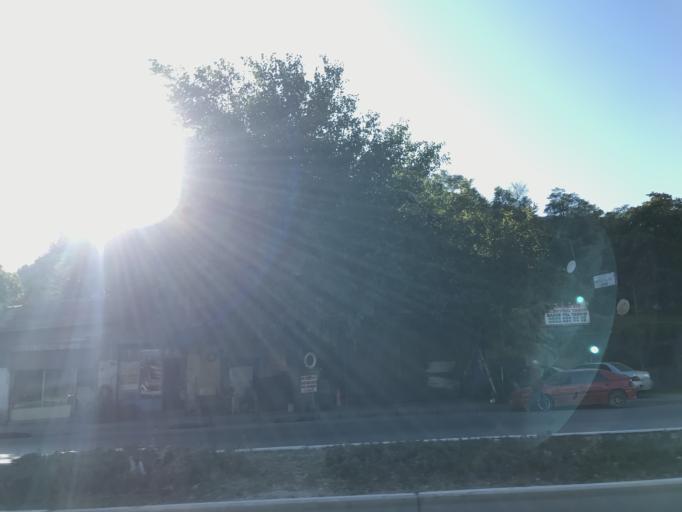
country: TR
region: Ankara
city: Ankara
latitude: 39.9477
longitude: 32.8615
